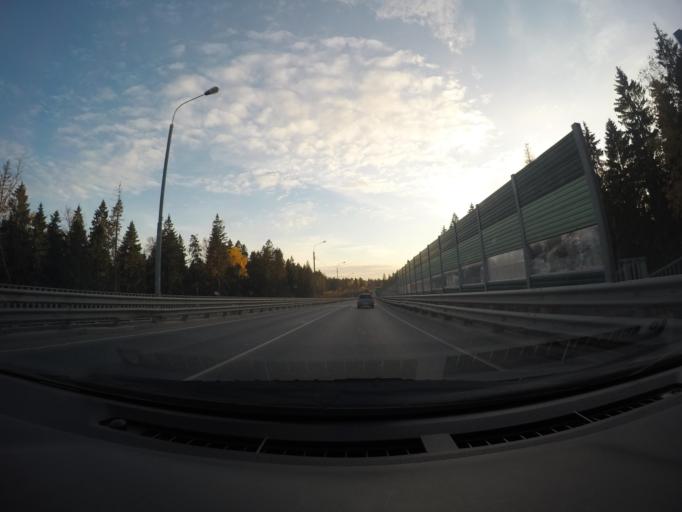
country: RU
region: Moskovskaya
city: Firsanovka
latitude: 55.9566
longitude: 37.2611
